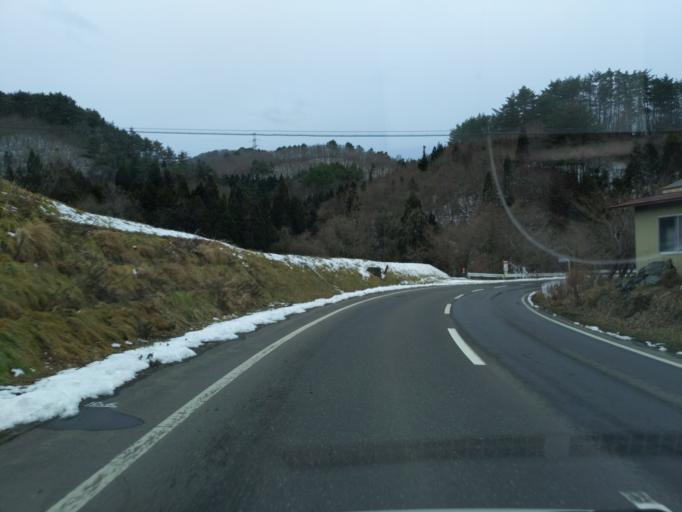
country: JP
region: Iwate
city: Mizusawa
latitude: 39.1051
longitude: 141.2742
